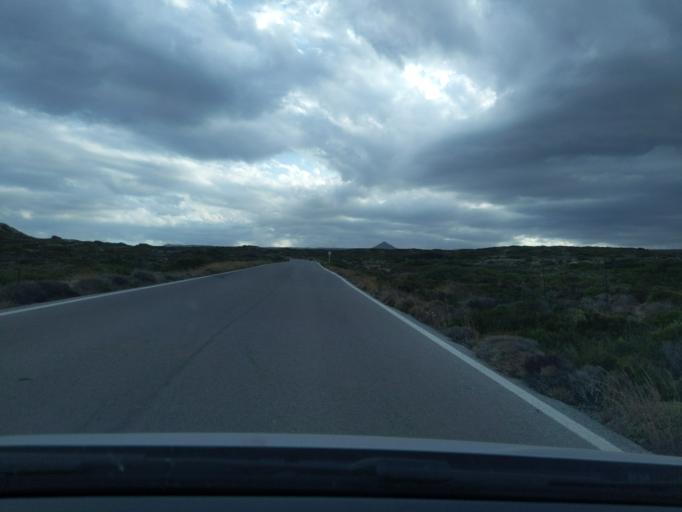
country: GR
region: Crete
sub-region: Nomos Lasithiou
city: Palekastro
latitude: 35.2453
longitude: 26.2493
